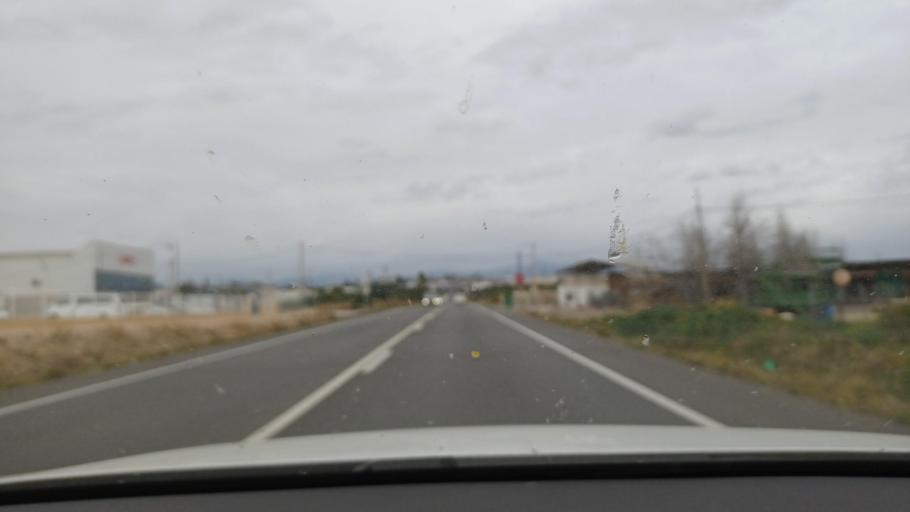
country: ES
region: Catalonia
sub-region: Provincia de Tarragona
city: Amposta
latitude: 40.6979
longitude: 0.5723
